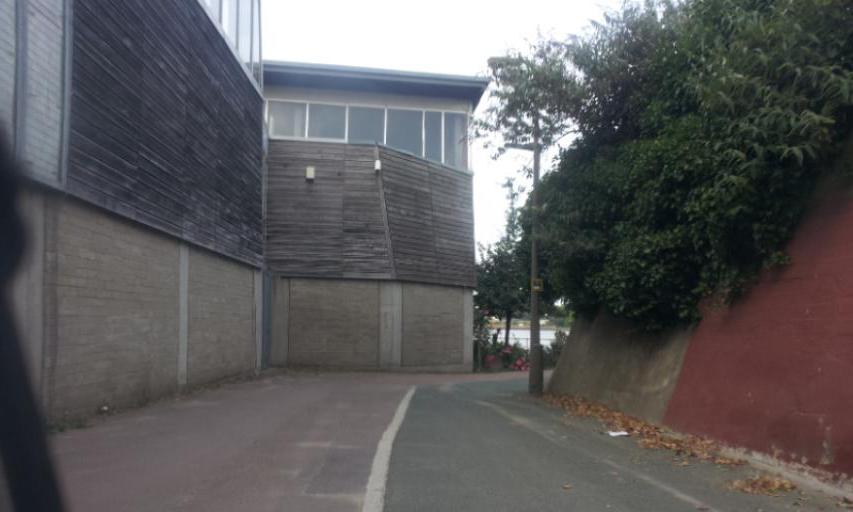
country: GB
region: England
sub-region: Greater London
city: Blackheath
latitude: 51.4942
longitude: 0.0187
